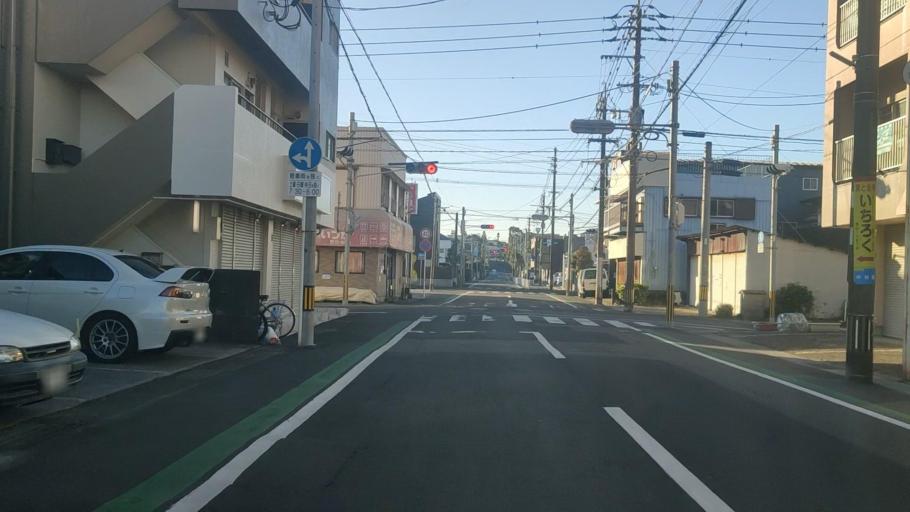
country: JP
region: Miyazaki
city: Miyazaki-shi
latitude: 31.9003
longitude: 131.4169
